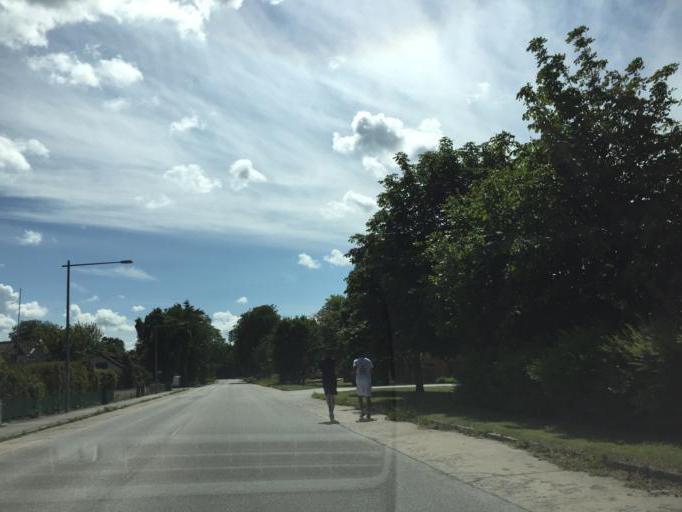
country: SE
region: Gotland
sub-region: Gotland
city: Visby
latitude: 57.6145
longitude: 18.2849
